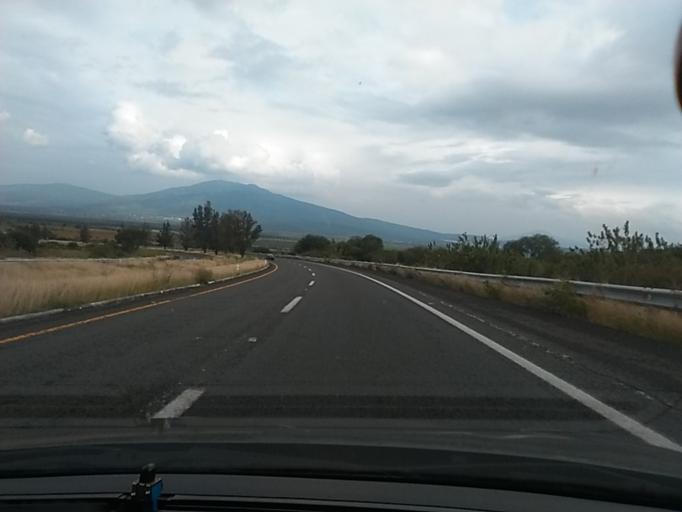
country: MX
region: Michoacan
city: Ixtlan
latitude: 20.1877
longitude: -102.3097
